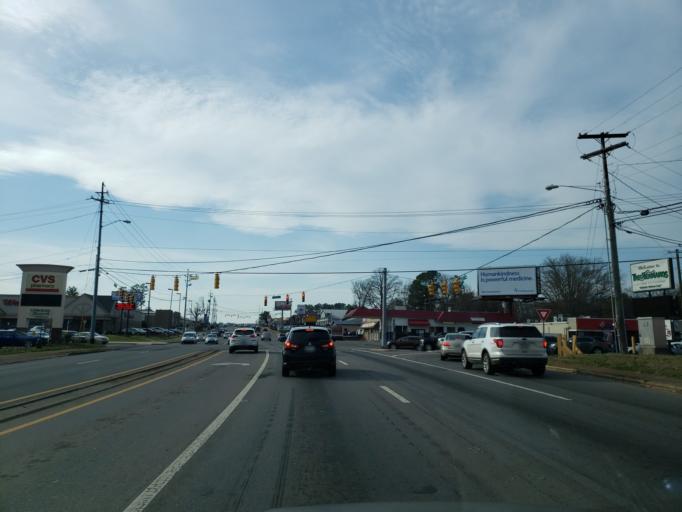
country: US
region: Tennessee
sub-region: Bradley County
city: East Cleveland
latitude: 35.1783
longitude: -84.8640
